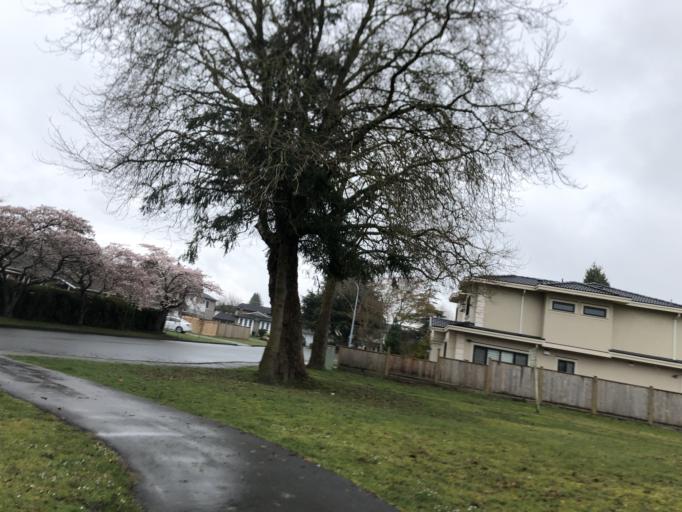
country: CA
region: British Columbia
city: Richmond
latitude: 49.1454
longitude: -123.1310
